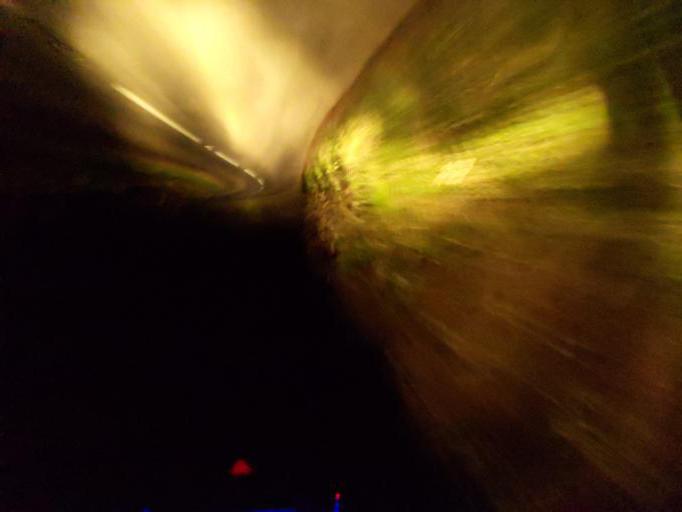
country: GB
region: England
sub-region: Cornwall
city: Saltash
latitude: 50.3630
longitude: -4.2921
